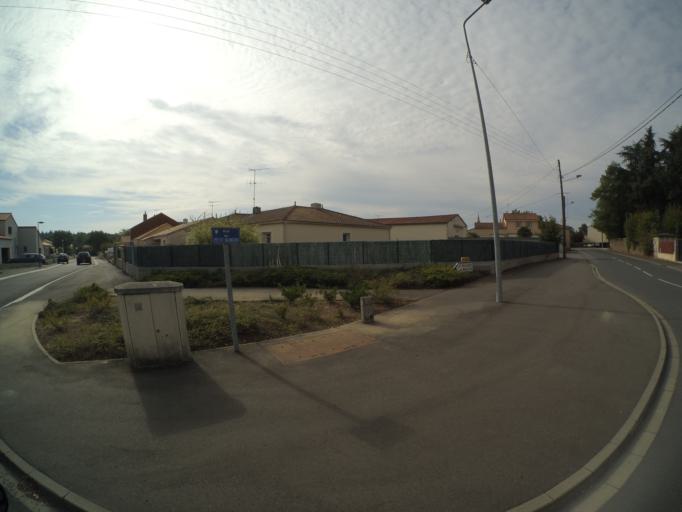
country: FR
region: Pays de la Loire
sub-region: Departement de Maine-et-Loire
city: Villedieu-la-Blouere
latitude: 47.1519
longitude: -1.0587
